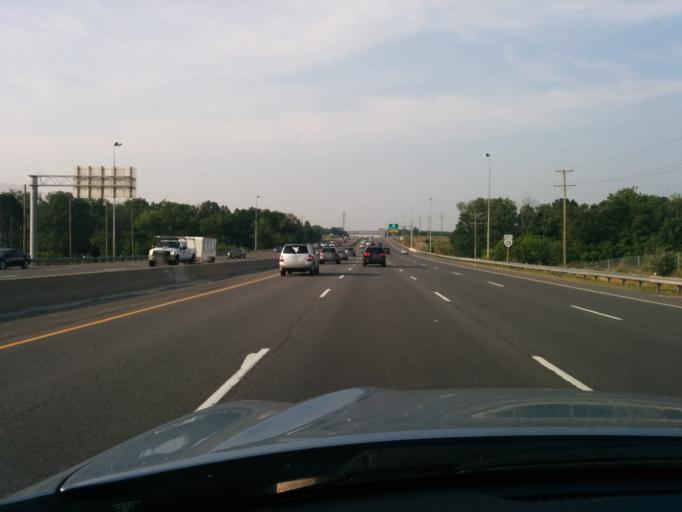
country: US
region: Virginia
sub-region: Loudoun County
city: Sterling
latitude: 39.0188
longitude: -77.4320
